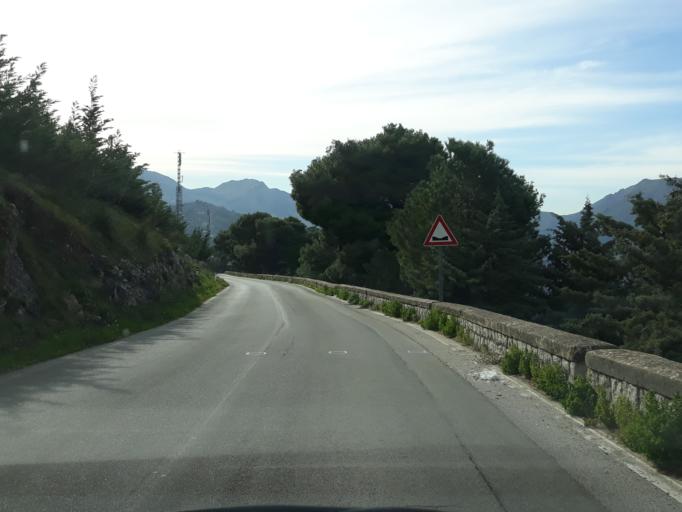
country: IT
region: Sicily
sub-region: Palermo
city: Piano Maglio-Blandino
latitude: 38.0448
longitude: 13.3078
